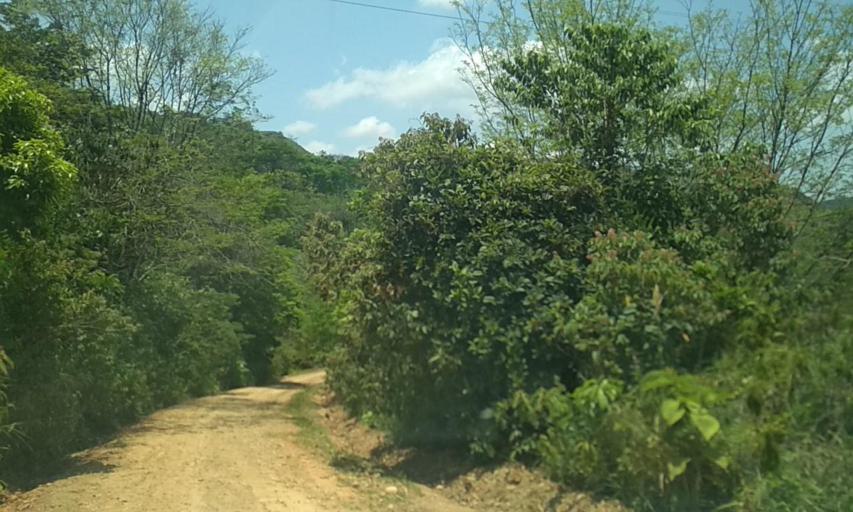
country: MX
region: Chiapas
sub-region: Tecpatan
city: Raudales Malpaso
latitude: 17.3936
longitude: -93.7377
